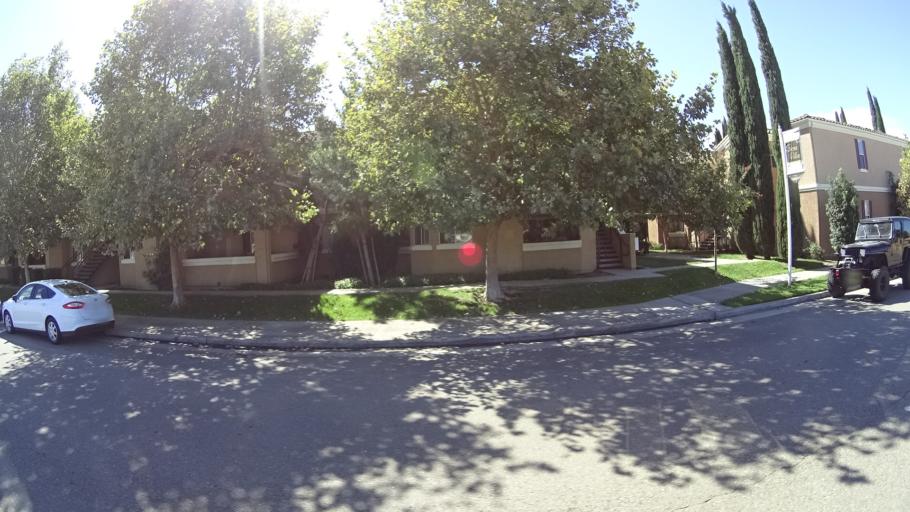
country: US
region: California
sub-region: Sacramento County
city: Laguna
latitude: 38.4265
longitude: -121.4730
